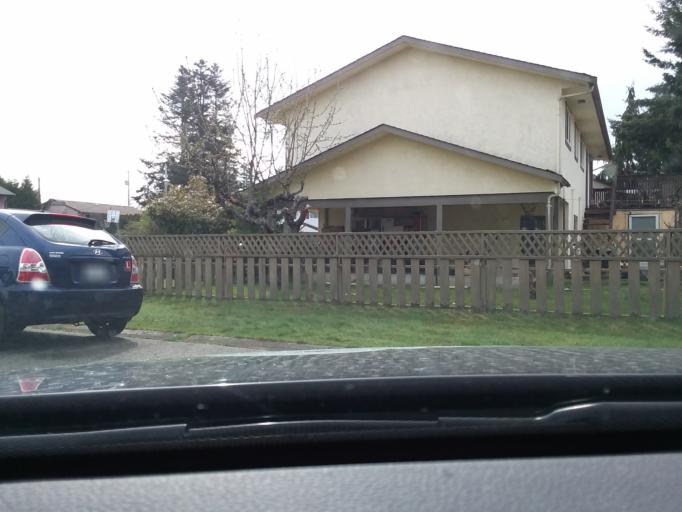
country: CA
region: British Columbia
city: Oak Bay
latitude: 48.4753
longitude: -123.3314
